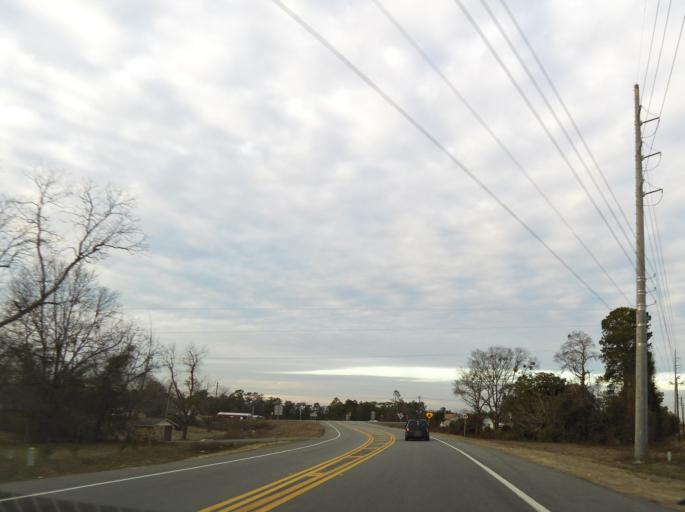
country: US
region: Georgia
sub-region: Houston County
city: Centerville
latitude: 32.6728
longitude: -83.7084
